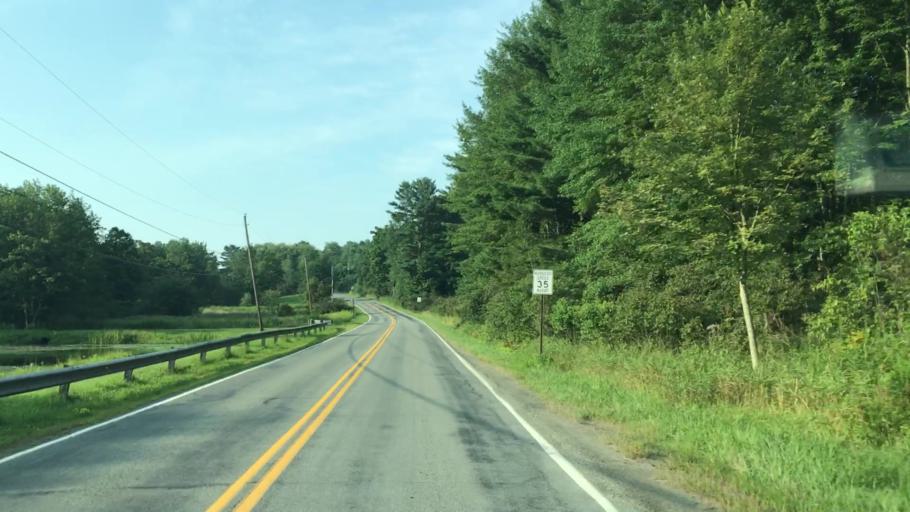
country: US
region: Pennsylvania
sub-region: Lackawanna County
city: Dalton
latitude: 41.6070
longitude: -75.7142
